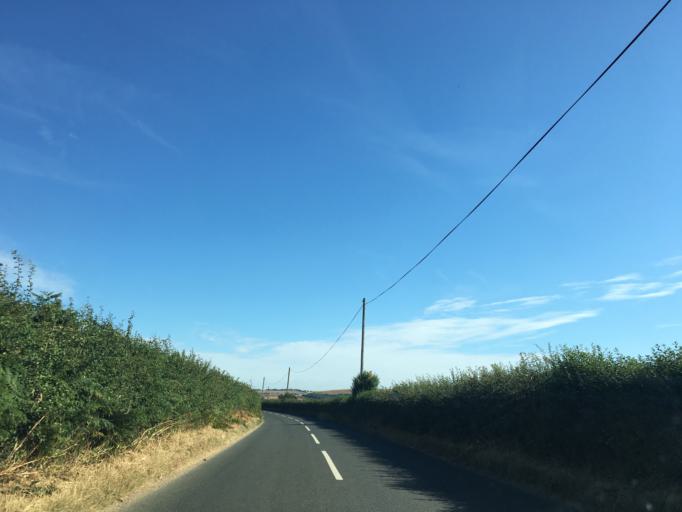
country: GB
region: England
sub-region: Isle of Wight
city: Chale
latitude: 50.6239
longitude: -1.3206
